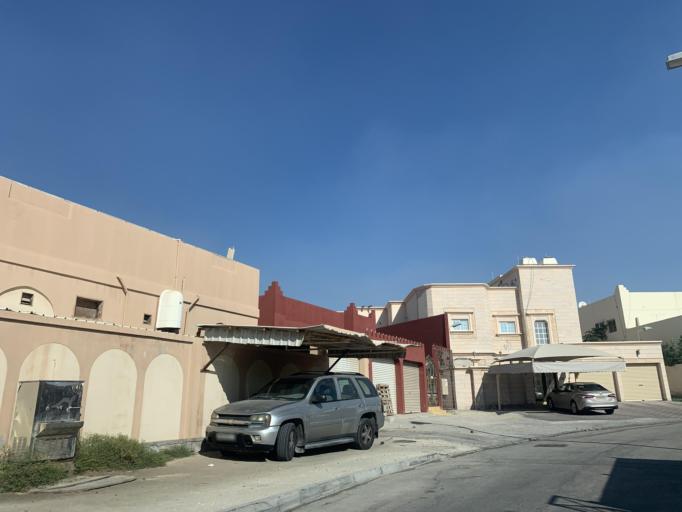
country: BH
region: Central Governorate
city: Madinat Hamad
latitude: 26.1163
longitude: 50.5053
